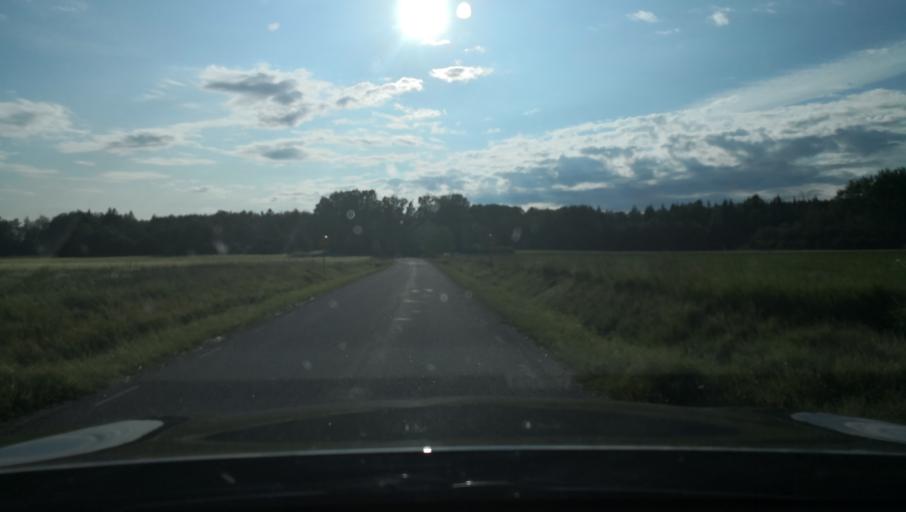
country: SE
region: Uppsala
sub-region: Osthammars Kommun
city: Osterbybruk
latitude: 60.0200
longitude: 17.9654
